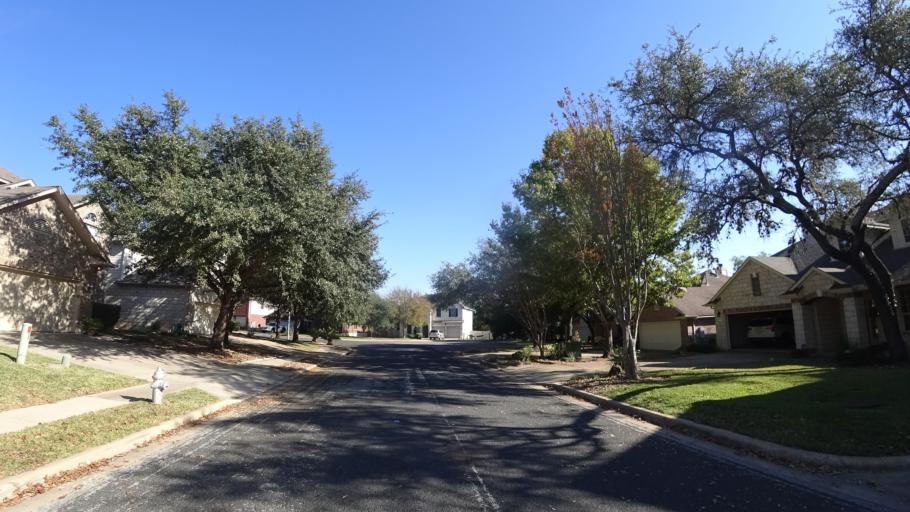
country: US
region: Texas
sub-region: Travis County
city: Barton Creek
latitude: 30.2252
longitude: -97.8766
